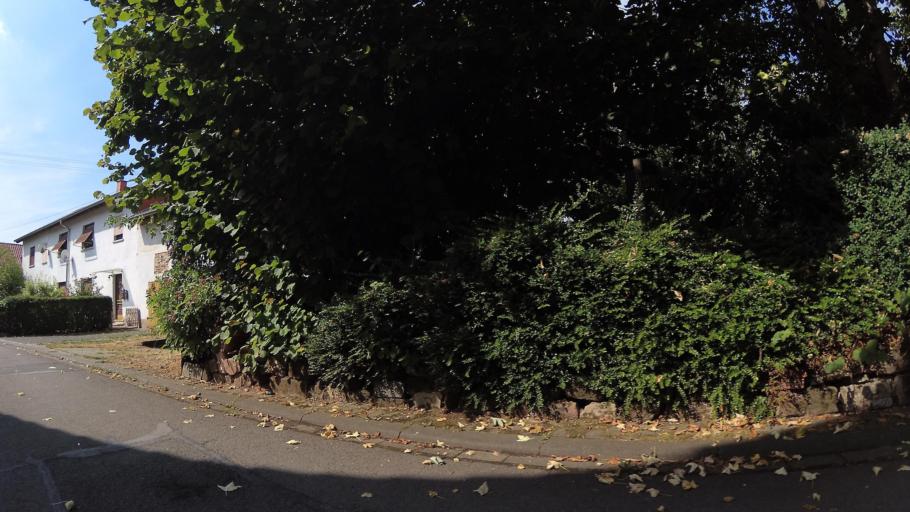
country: DE
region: Rheinland-Pfalz
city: Grossbundenbach
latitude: 49.3076
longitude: 7.4214
